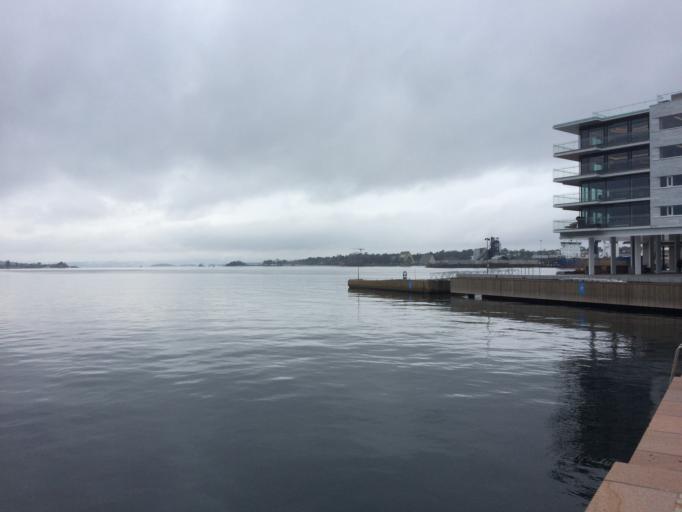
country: NO
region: Oslo
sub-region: Oslo
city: Oslo
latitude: 59.9062
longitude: 10.7211
